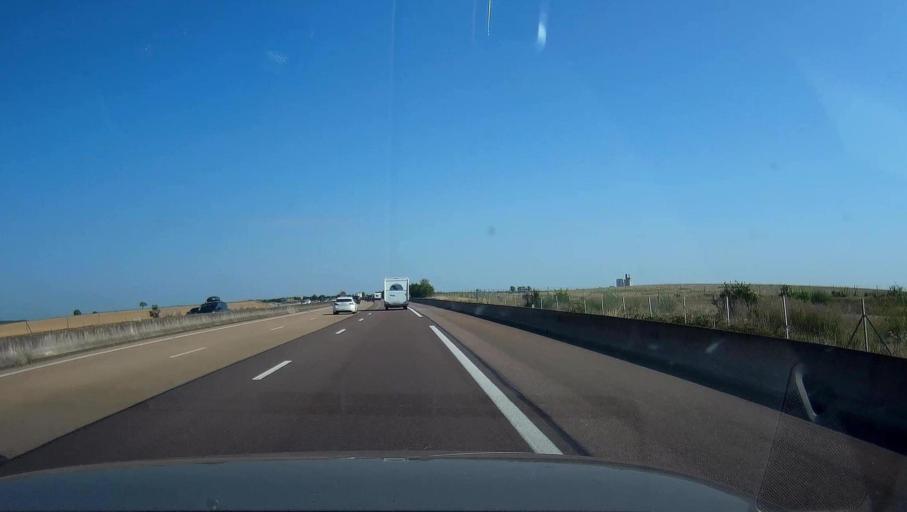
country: FR
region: Bourgogne
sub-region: Departement de la Cote-d'Or
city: Marcilly-sur-Tille
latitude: 47.4759
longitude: 5.1893
